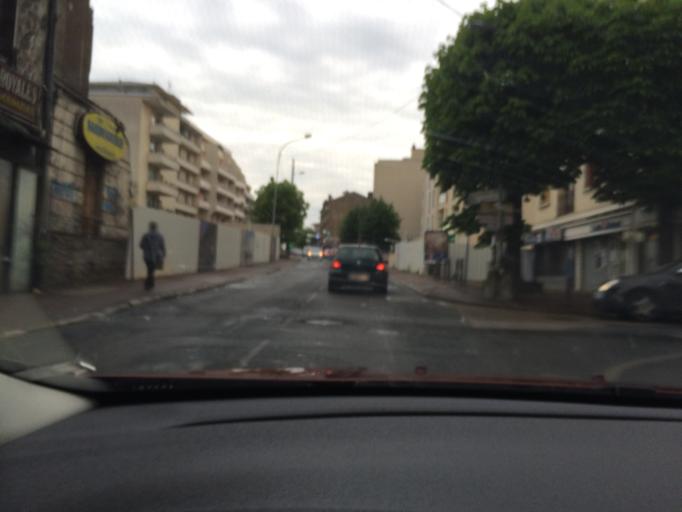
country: FR
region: Ile-de-France
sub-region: Departement du Val-d'Oise
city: Ermont
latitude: 48.9821
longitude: 2.2714
